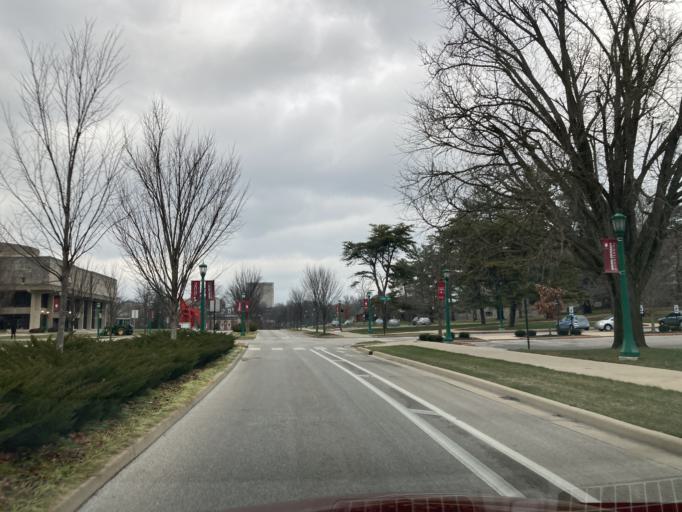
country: US
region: Indiana
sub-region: Monroe County
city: Bloomington
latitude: 39.1650
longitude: -86.5164
